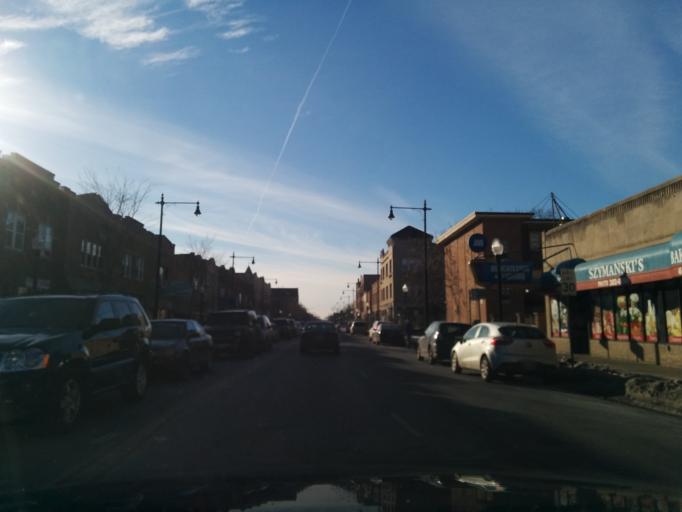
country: US
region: Illinois
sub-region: Cook County
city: Harwood Heights
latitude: 41.9531
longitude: -87.7773
